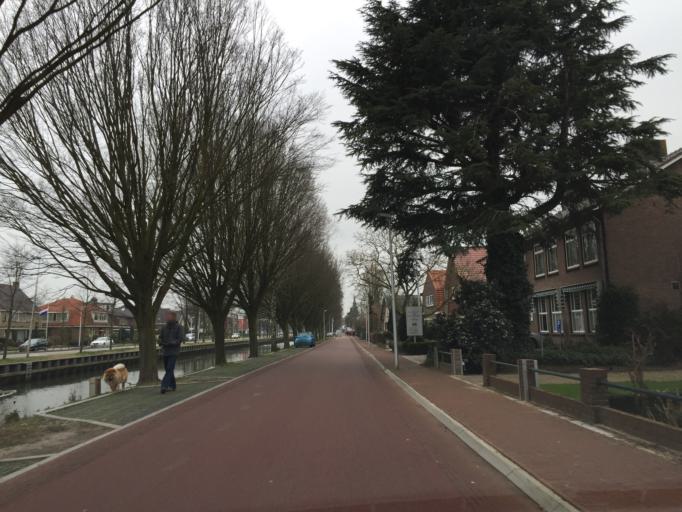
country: NL
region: Utrecht
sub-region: Stichtse Vecht
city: Maarssen
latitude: 52.0819
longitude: 5.0433
